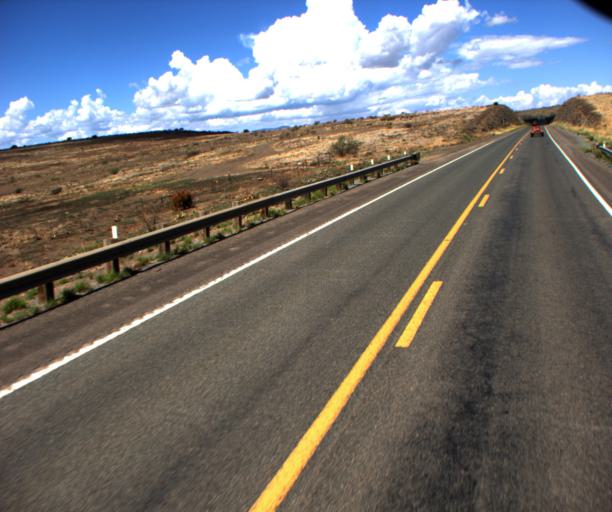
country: US
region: Arizona
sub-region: Yavapai County
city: Camp Verde
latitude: 34.5155
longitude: -112.0213
